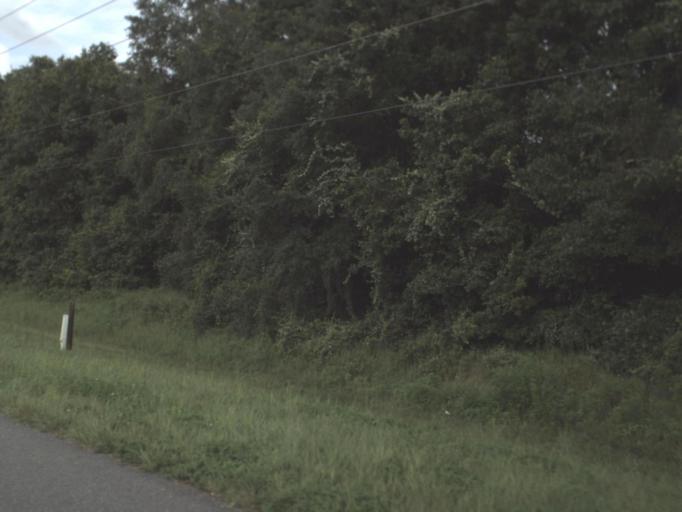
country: US
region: Florida
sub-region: Hernando County
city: Ridge Manor
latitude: 28.4952
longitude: -82.1735
